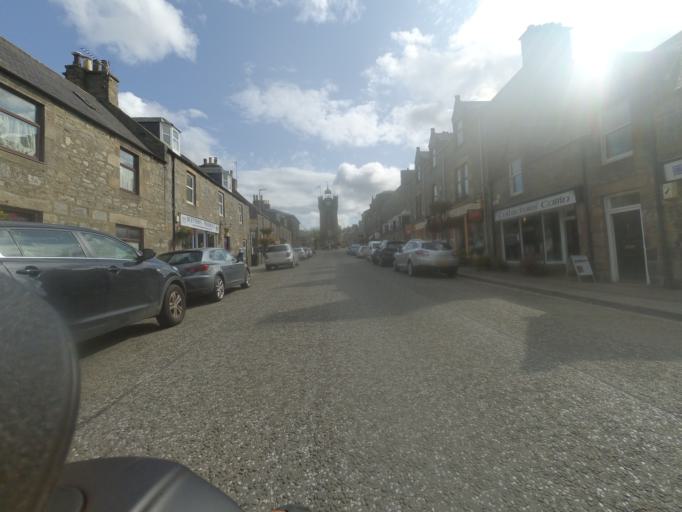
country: GB
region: Scotland
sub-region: Moray
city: Dufftown
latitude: 57.4457
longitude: -3.1286
